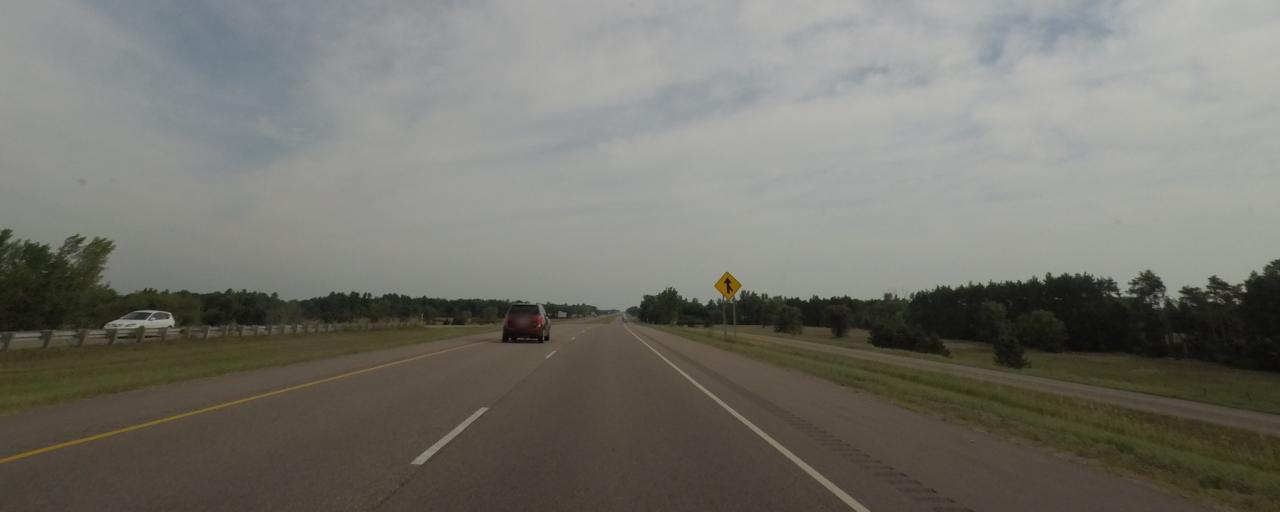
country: US
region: Wisconsin
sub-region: Portage County
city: Plover
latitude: 44.2144
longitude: -89.5244
